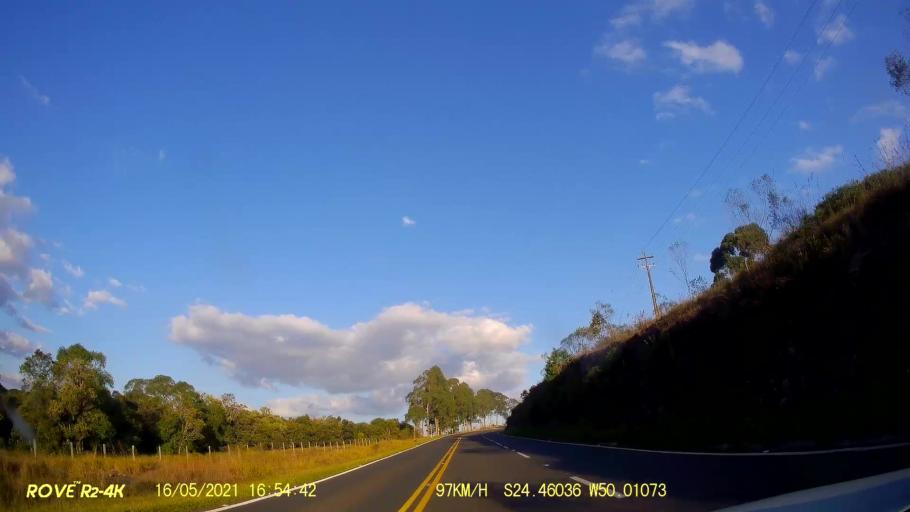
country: BR
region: Parana
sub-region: Pirai Do Sul
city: Pirai do Sul
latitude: -24.4603
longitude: -50.0107
